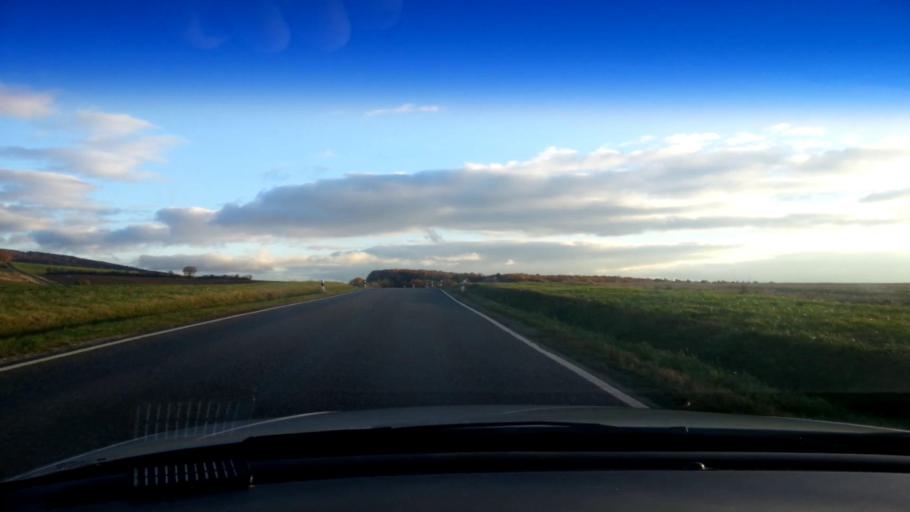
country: DE
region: Bavaria
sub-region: Upper Franconia
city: Hirschaid
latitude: 49.8519
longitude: 11.0181
